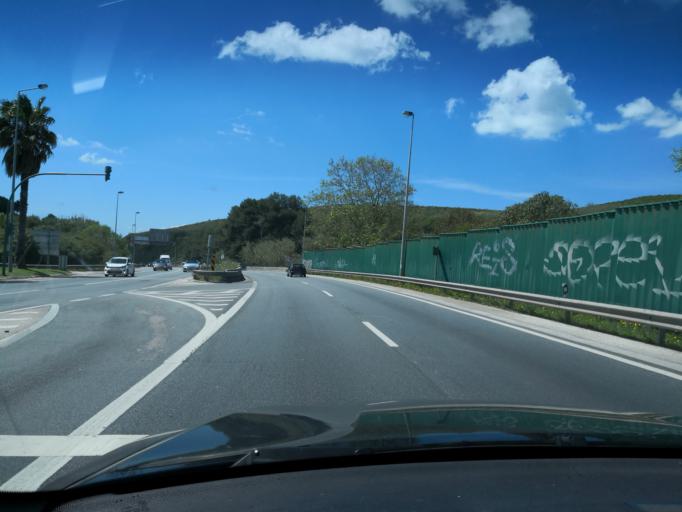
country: PT
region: Setubal
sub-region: Almada
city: Costa de Caparica
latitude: 38.6527
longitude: -9.2270
